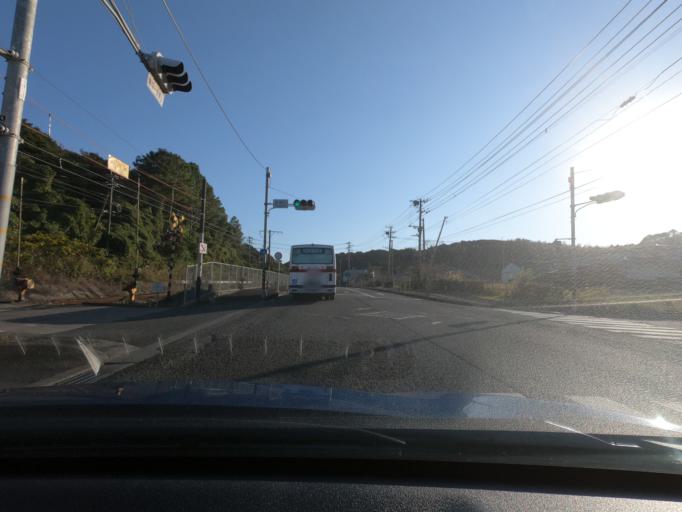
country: JP
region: Kagoshima
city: Akune
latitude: 32.0018
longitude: 130.1961
